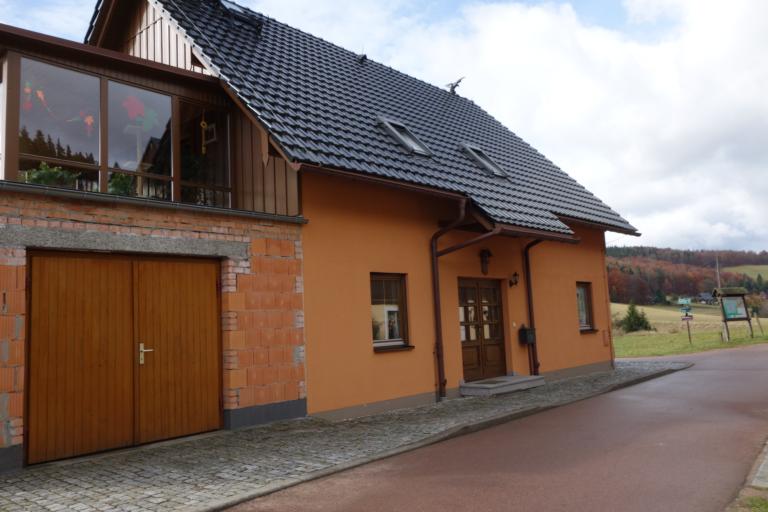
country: DE
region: Saxony
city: Altenberg
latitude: 50.7258
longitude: 13.7090
